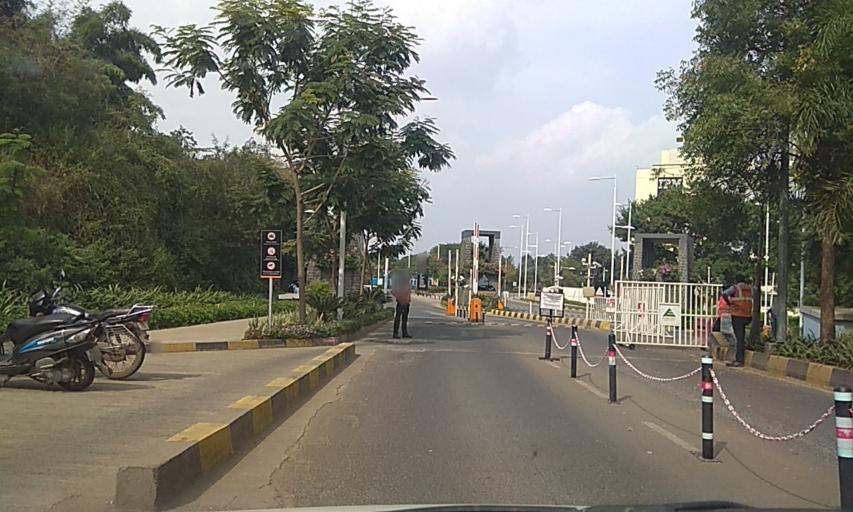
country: IN
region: Maharashtra
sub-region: Pune Division
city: Pimpri
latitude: 18.6022
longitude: 73.7153
